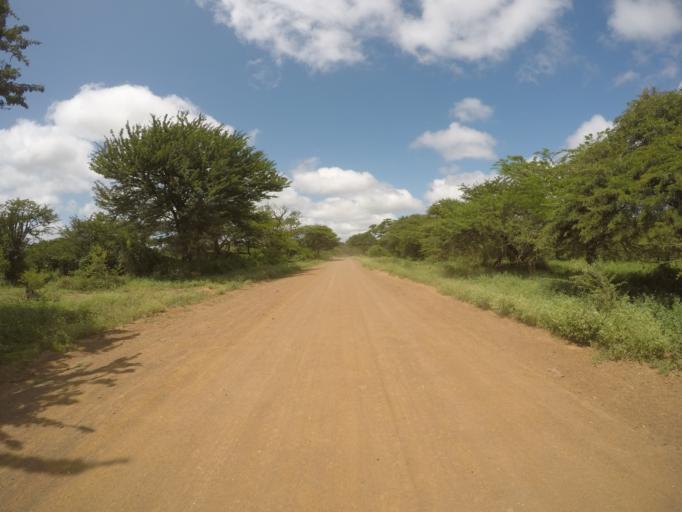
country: ZA
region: KwaZulu-Natal
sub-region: uThungulu District Municipality
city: Empangeni
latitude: -28.5692
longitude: 31.8363
